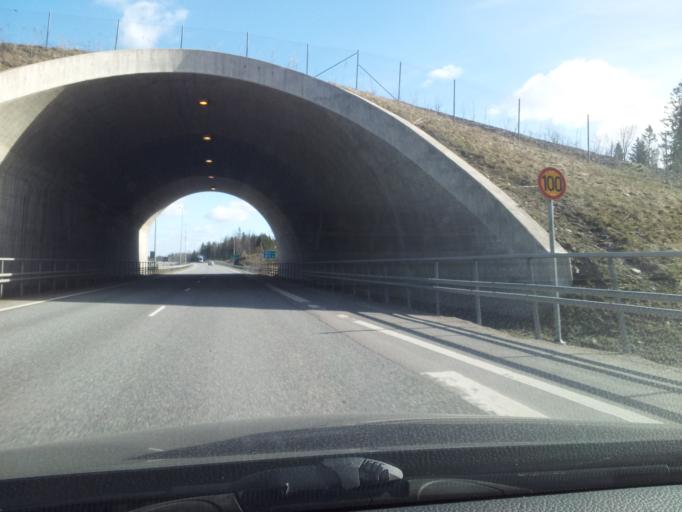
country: FI
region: Uusimaa
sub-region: Helsinki
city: Kirkkonummi
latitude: 60.1395
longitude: 24.5461
